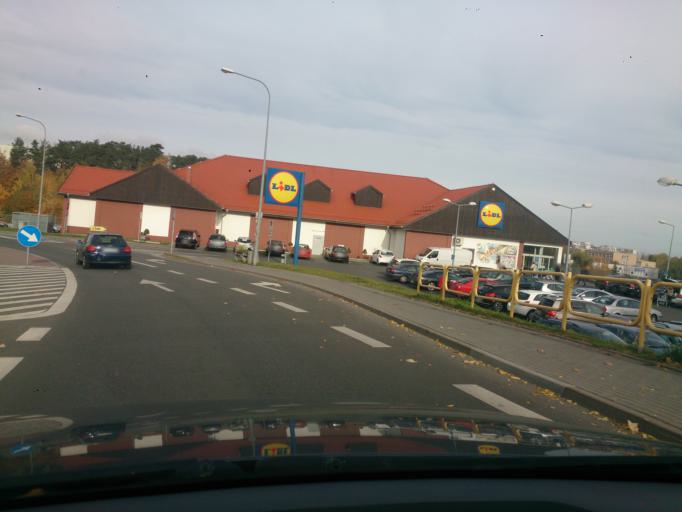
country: PL
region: Pomeranian Voivodeship
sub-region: Gdynia
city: Wielki Kack
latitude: 54.4694
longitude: 18.4917
